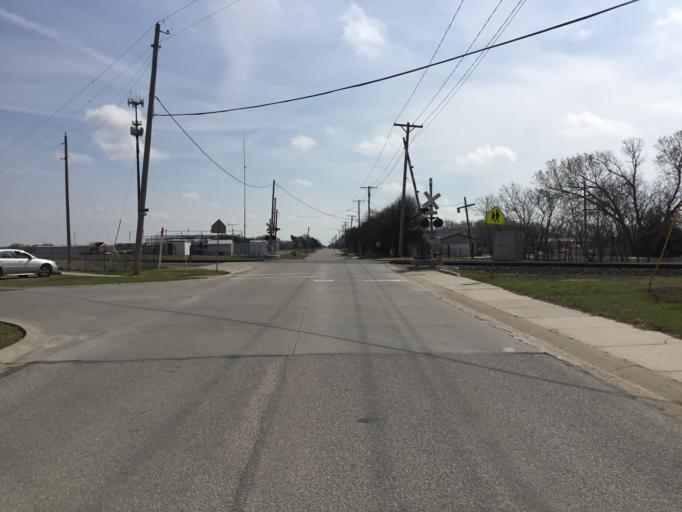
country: US
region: Kansas
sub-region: Butler County
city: Rose Hill
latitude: 37.5631
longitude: -97.1322
